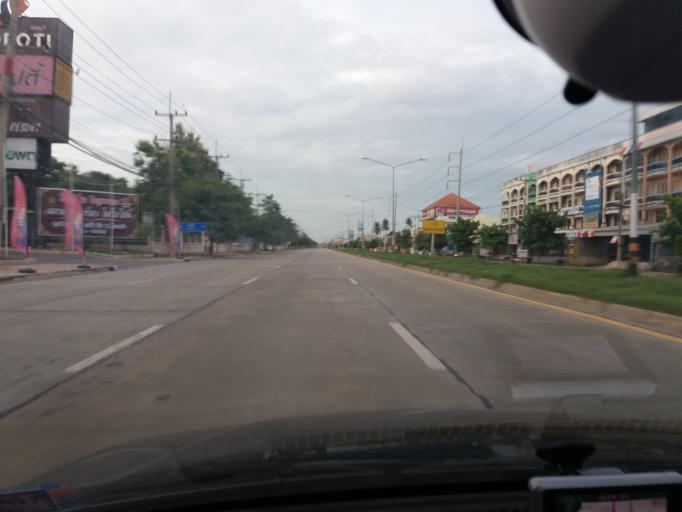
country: TH
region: Suphan Buri
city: U Thong
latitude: 14.3911
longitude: 99.8954
